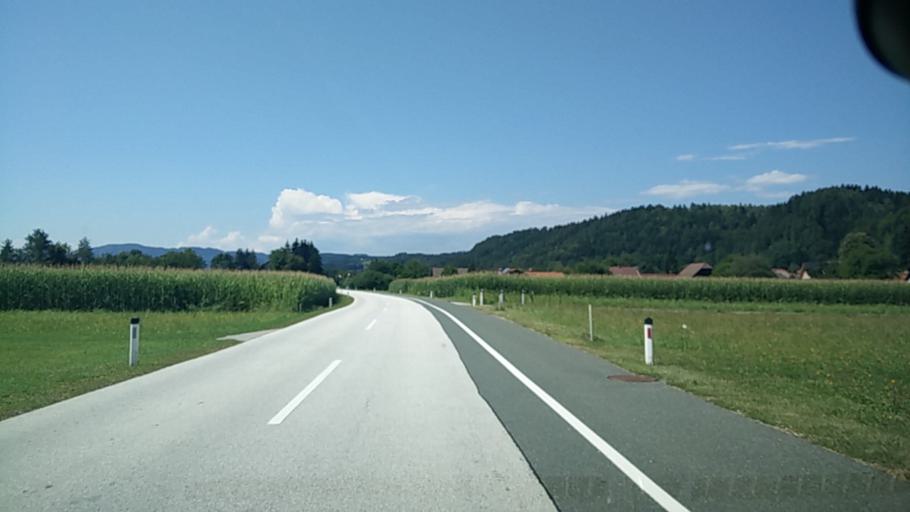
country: AT
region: Carinthia
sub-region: Politischer Bezirk Volkermarkt
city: Sittersdorf
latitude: 46.5487
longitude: 14.5874
